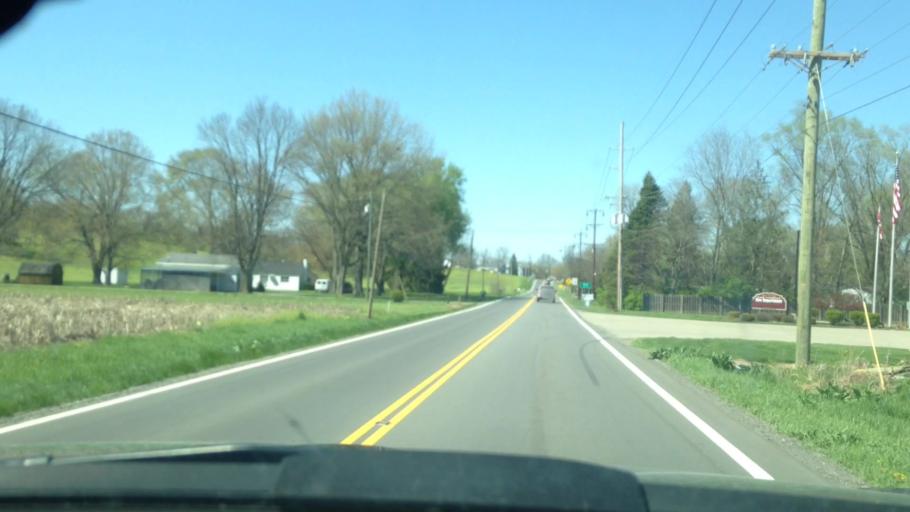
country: US
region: Ohio
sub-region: Butler County
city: Ross
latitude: 39.3830
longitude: -84.6556
